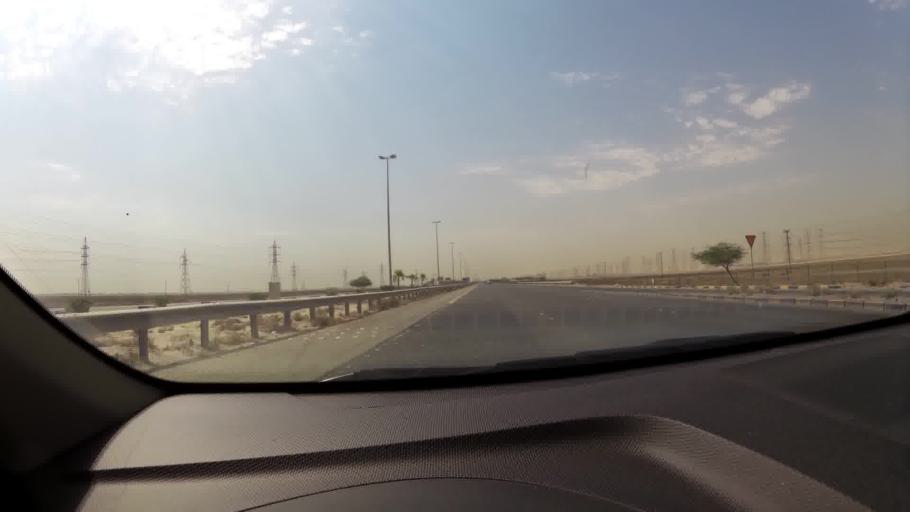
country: KW
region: Al Ahmadi
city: Al Fahahil
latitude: 28.8495
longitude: 48.2449
